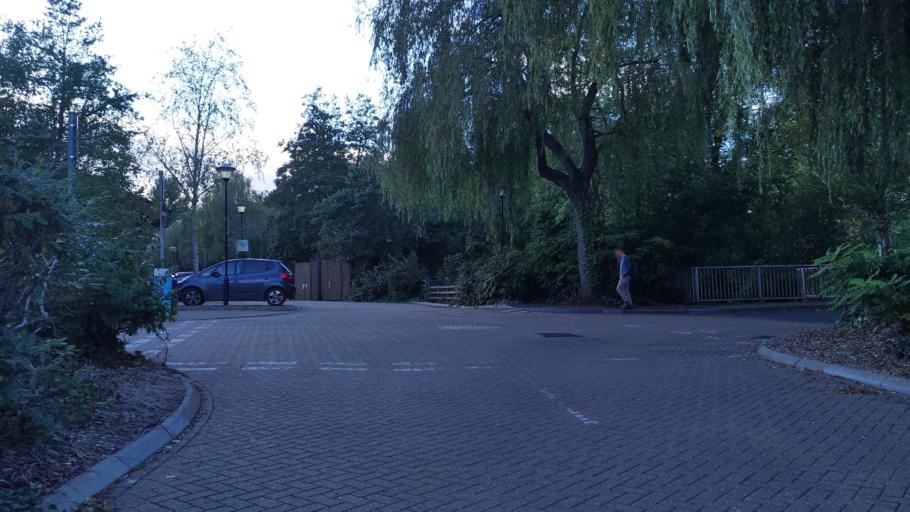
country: GB
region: England
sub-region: Somerset
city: Yeovil
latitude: 50.9367
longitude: -2.6358
